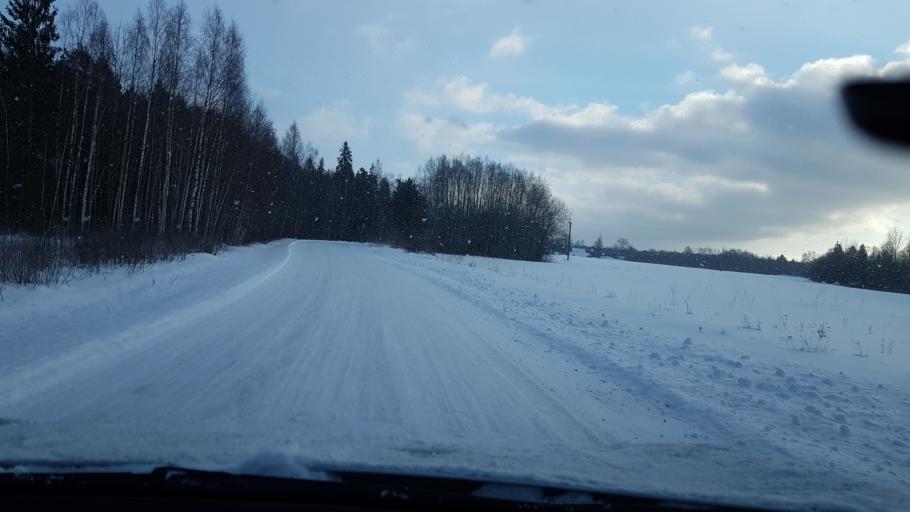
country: EE
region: Harju
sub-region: Nissi vald
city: Turba
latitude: 59.1697
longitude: 24.1380
